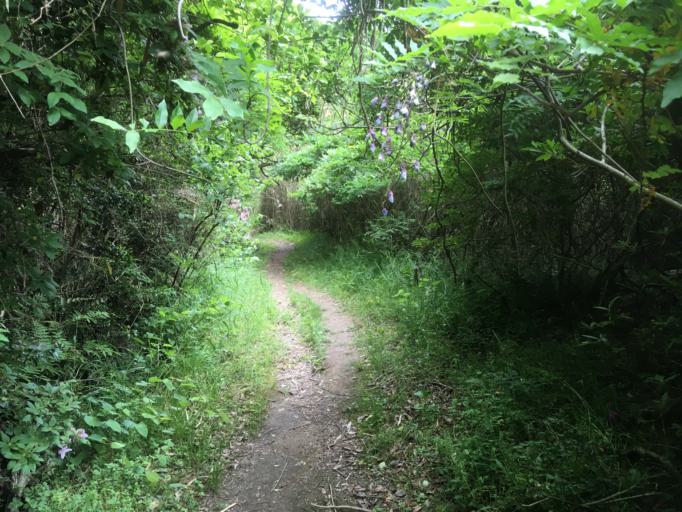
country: JP
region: Nara
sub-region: Ikoma-shi
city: Ikoma
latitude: 34.7030
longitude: 135.6718
